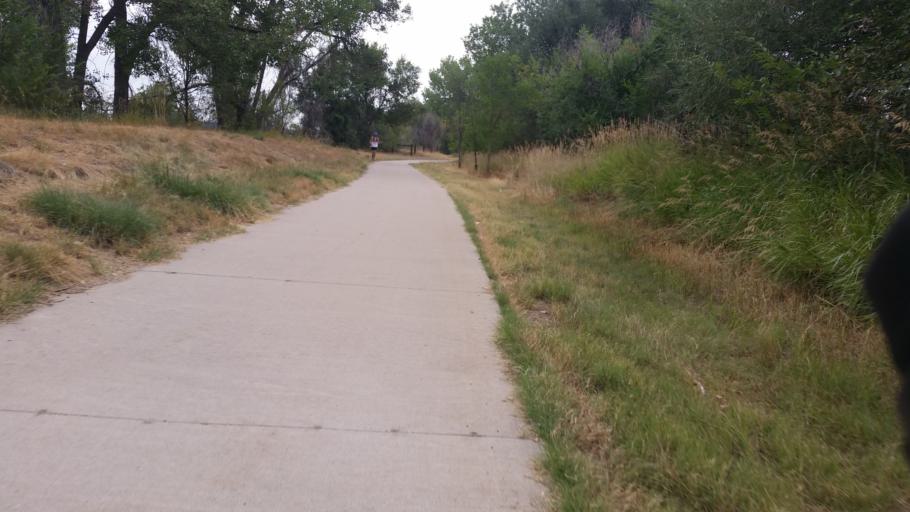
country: US
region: Colorado
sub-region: Adams County
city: Welby
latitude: 39.8259
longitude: -104.9669
